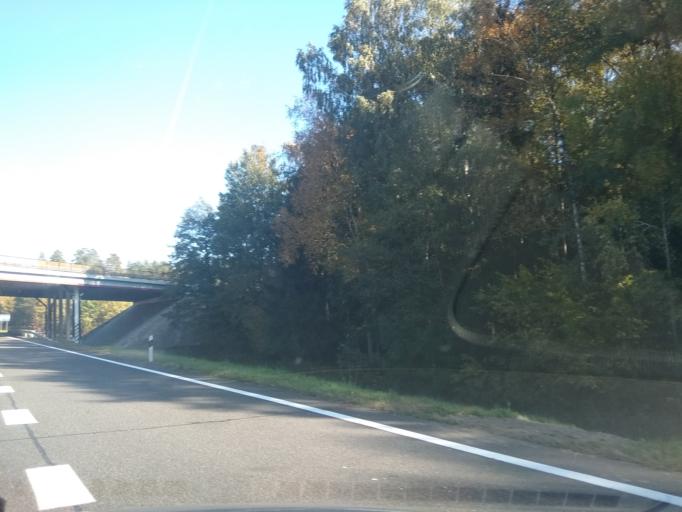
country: BY
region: Brest
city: Ivatsevichy
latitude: 52.8547
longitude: 25.6451
